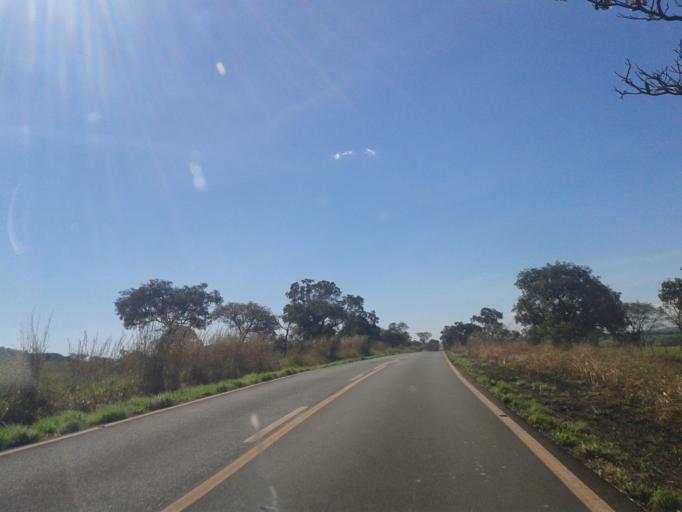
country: BR
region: Minas Gerais
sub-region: Ituiutaba
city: Ituiutaba
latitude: -19.1644
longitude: -49.7797
